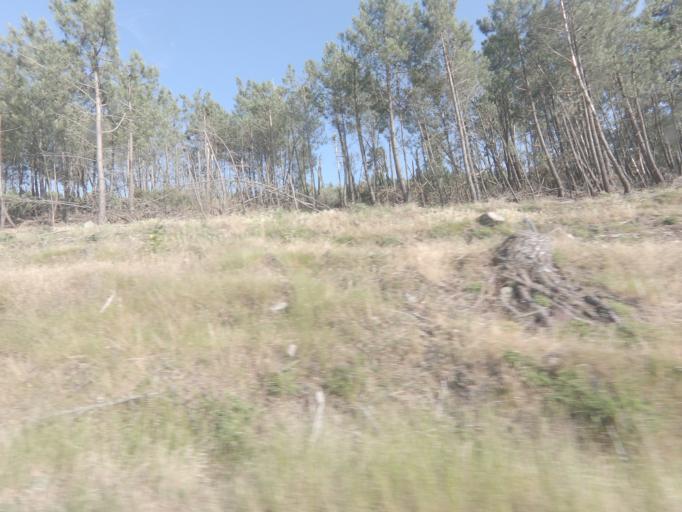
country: PT
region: Vila Real
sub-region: Sabrosa
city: Vilela
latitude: 41.1974
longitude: -7.6094
